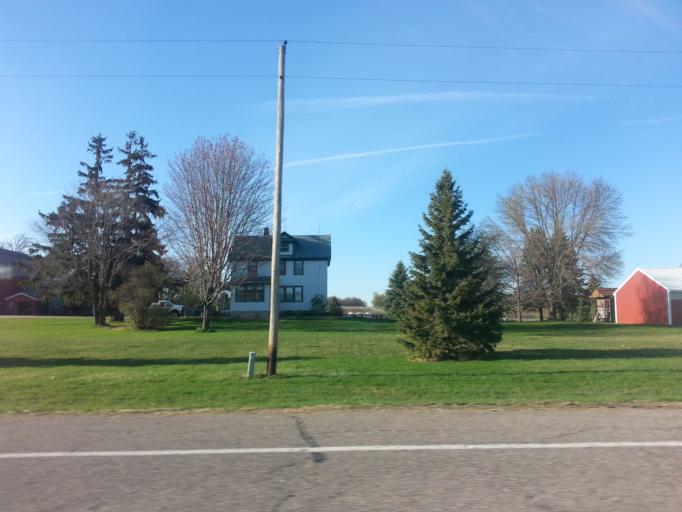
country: US
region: Minnesota
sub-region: Dakota County
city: Lakeville
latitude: 44.5871
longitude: -93.2337
